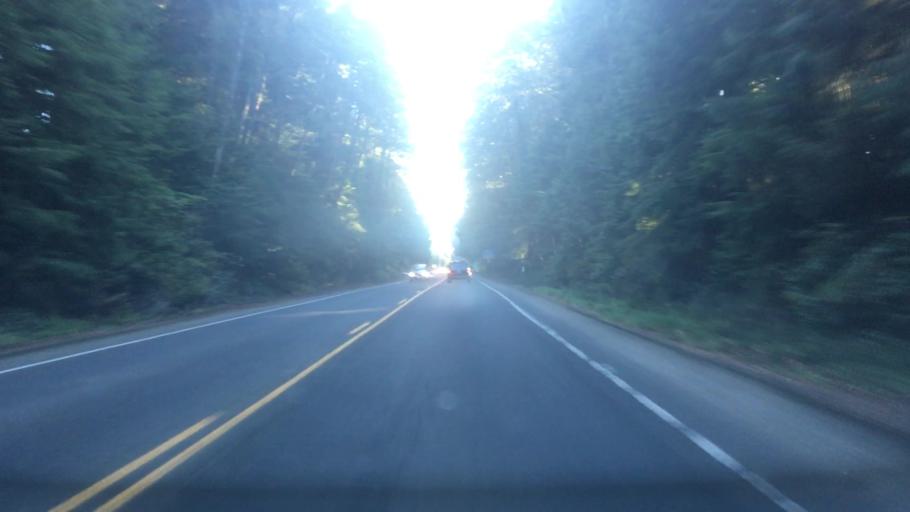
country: US
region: Oregon
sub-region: Clatsop County
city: Cannon Beach
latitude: 45.8921
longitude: -123.9565
